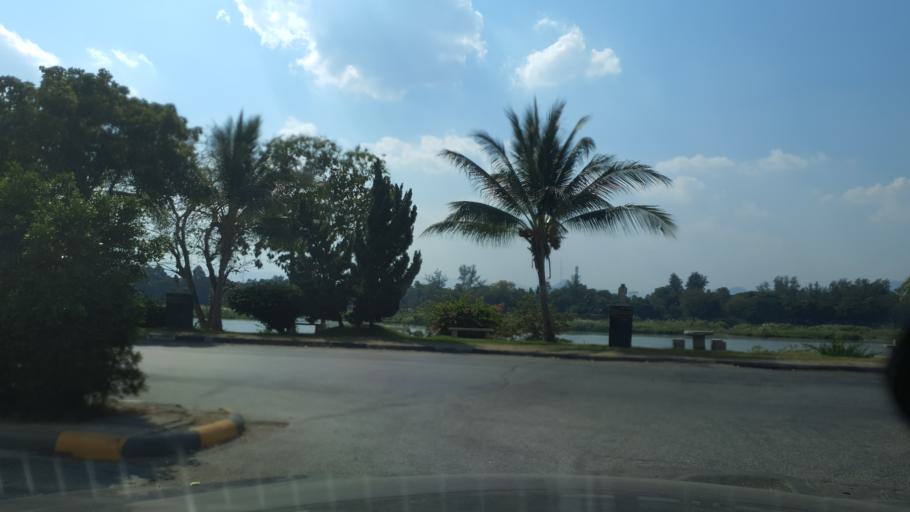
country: TH
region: Tak
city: Tak
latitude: 16.8727
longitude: 99.1228
